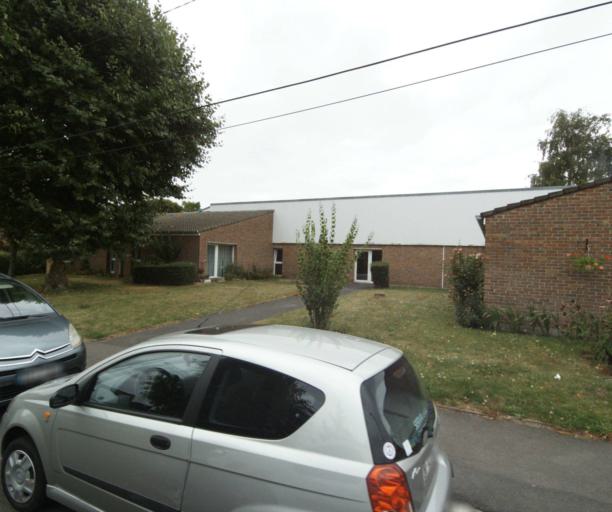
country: FR
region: Nord-Pas-de-Calais
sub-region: Departement du Nord
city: Leers
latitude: 50.6805
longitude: 3.2532
